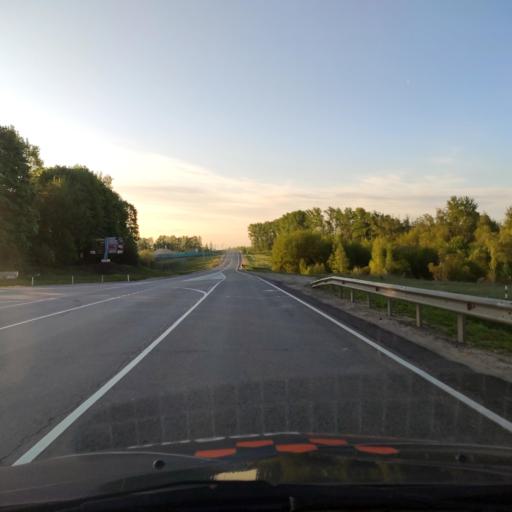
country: RU
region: Orjol
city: Livny
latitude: 52.4436
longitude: 37.5370
